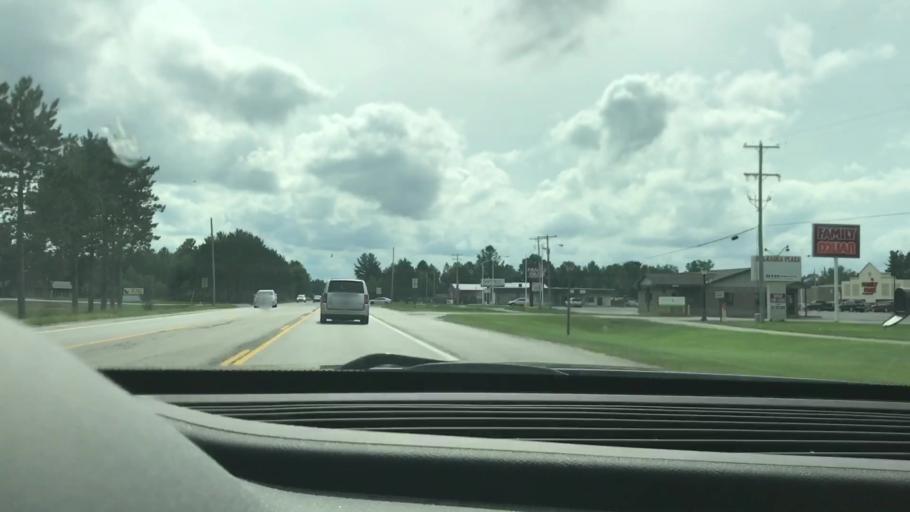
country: US
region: Michigan
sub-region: Kalkaska County
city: Kalkaska
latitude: 44.7225
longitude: -85.1853
